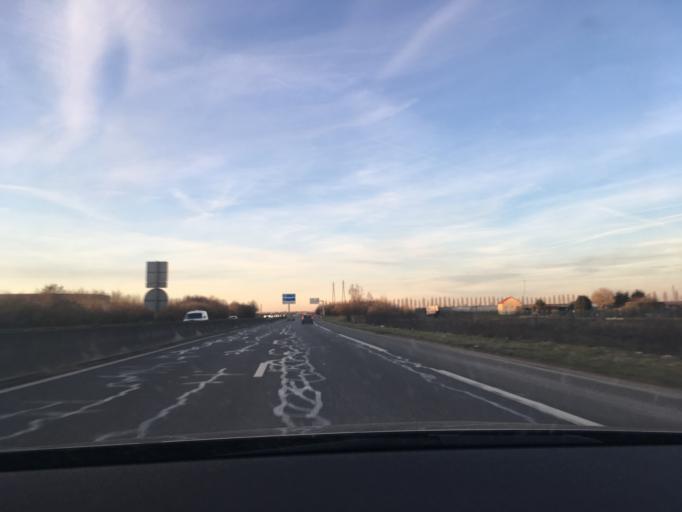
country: FR
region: Ile-de-France
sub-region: Departement de Seine-et-Marne
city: Vert-Saint-Denis
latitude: 48.5684
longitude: 2.6421
